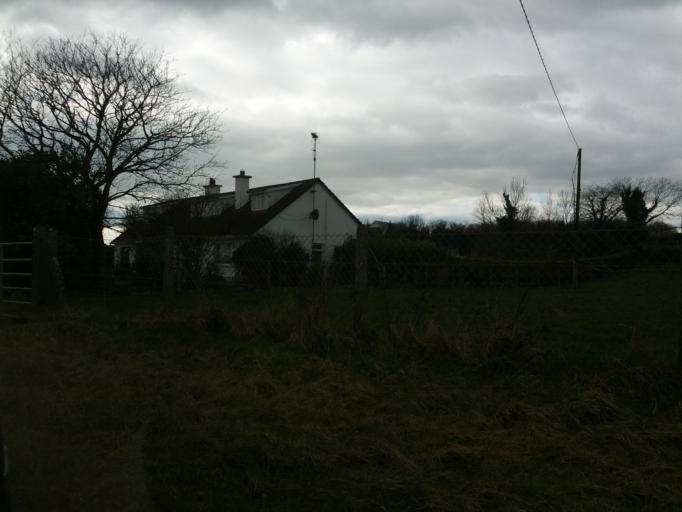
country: IE
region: Connaught
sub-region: County Galway
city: Athenry
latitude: 53.3903
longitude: -8.6438
